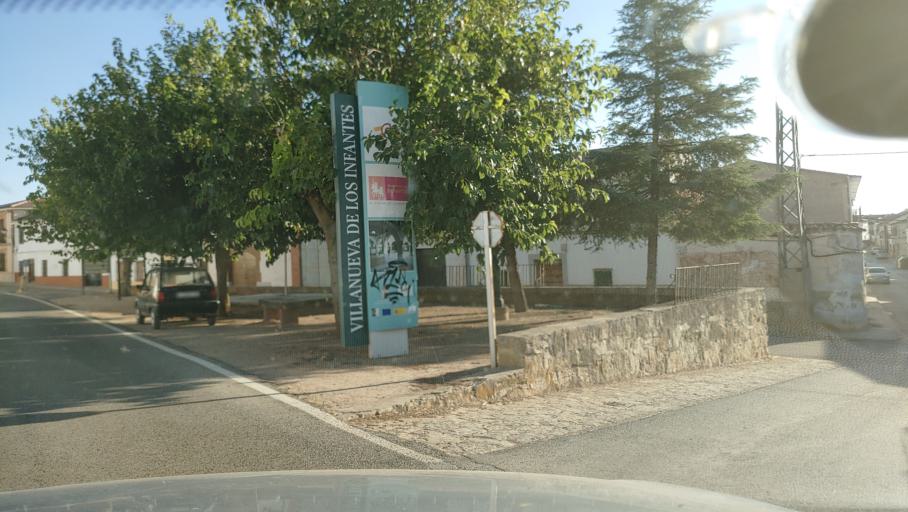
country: ES
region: Castille-La Mancha
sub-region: Provincia de Ciudad Real
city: Infantes
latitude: 38.7402
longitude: -3.0127
